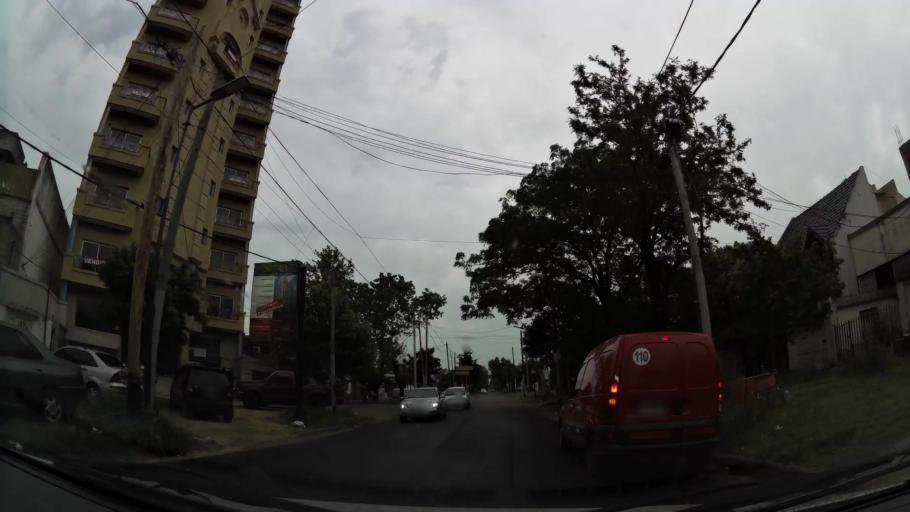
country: AR
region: Buenos Aires
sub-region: Partido de Lanus
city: Lanus
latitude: -34.6978
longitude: -58.3971
